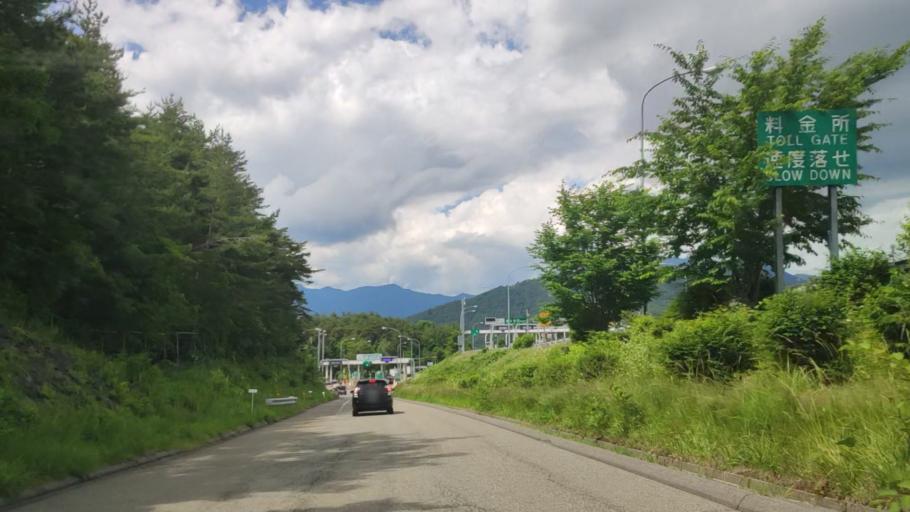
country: JP
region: Yamanashi
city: Fujikawaguchiko
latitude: 35.4789
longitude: 138.7717
